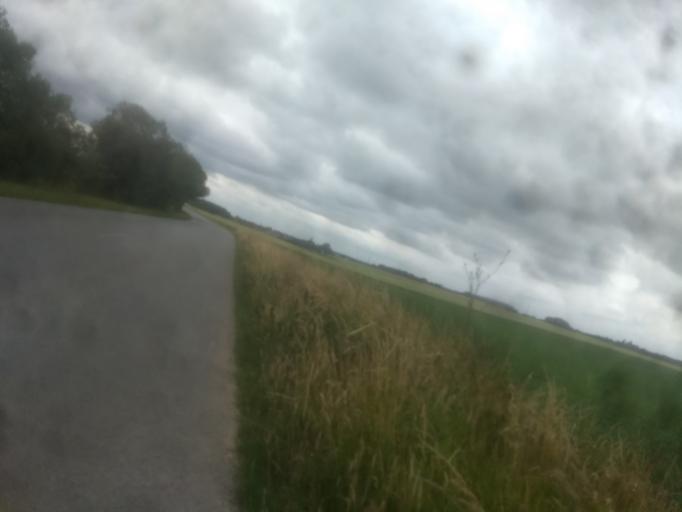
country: FR
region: Nord-Pas-de-Calais
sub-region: Departement du Pas-de-Calais
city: Thelus
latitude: 50.3379
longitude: 2.7947
